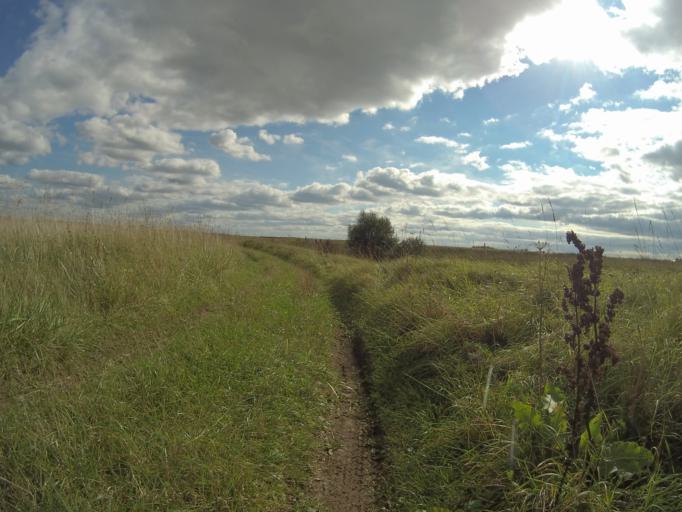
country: RU
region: Vladimir
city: Orgtrud
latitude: 56.3216
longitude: 40.6635
